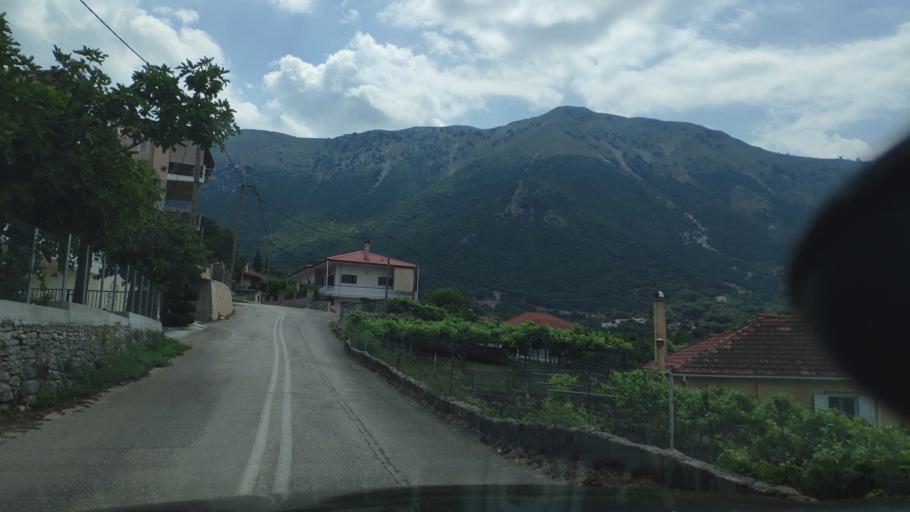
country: GR
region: Epirus
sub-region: Nomos Artas
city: Kampi
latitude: 39.2724
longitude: 20.9387
